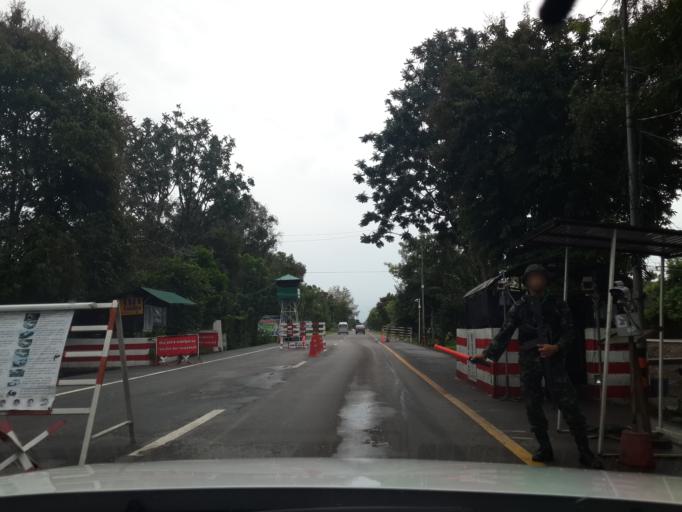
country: TH
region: Songkhla
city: Thepha
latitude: 6.8231
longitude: 101.0587
